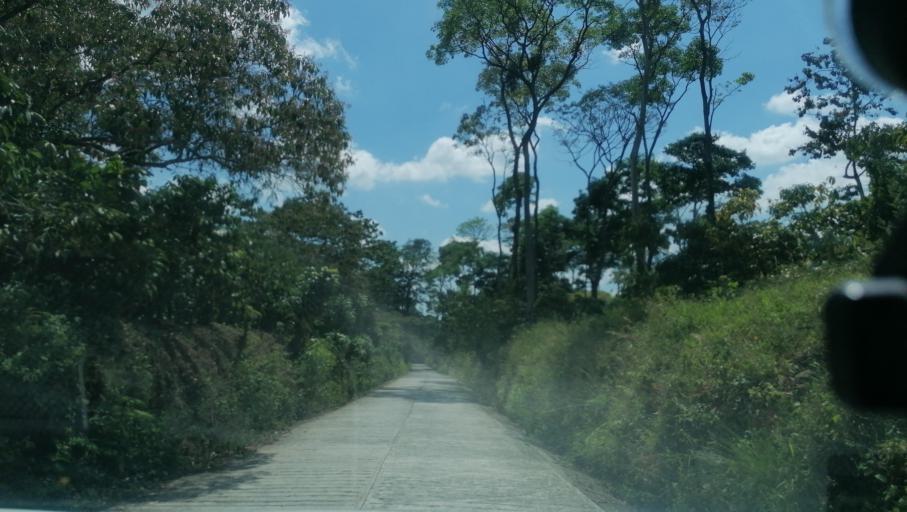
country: MX
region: Chiapas
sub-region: Union Juarez
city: Santo Domingo
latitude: 15.0393
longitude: -92.1441
